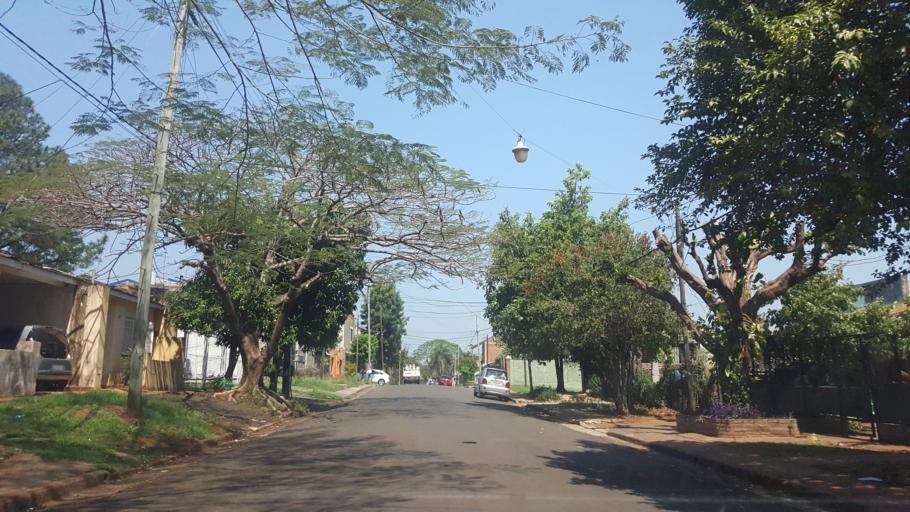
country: AR
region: Misiones
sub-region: Departamento de Capital
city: Posadas
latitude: -27.3700
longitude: -55.9156
